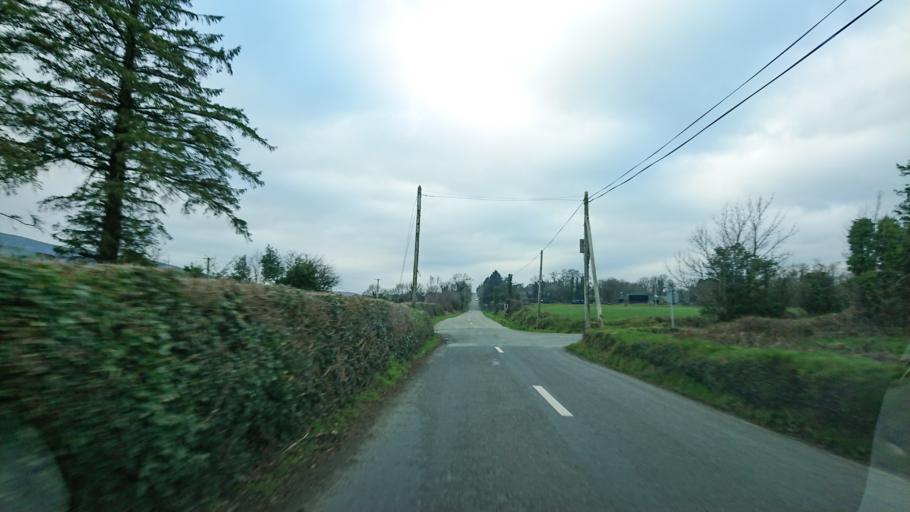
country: IE
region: Munster
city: Carrick-on-Suir
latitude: 52.3182
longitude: -7.5513
